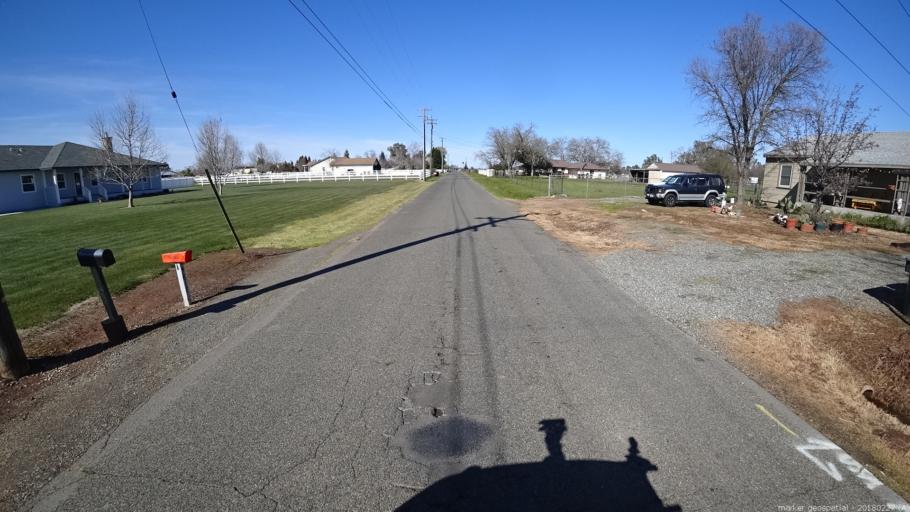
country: US
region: California
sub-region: Sacramento County
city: Elverta
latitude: 38.7110
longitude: -121.4458
